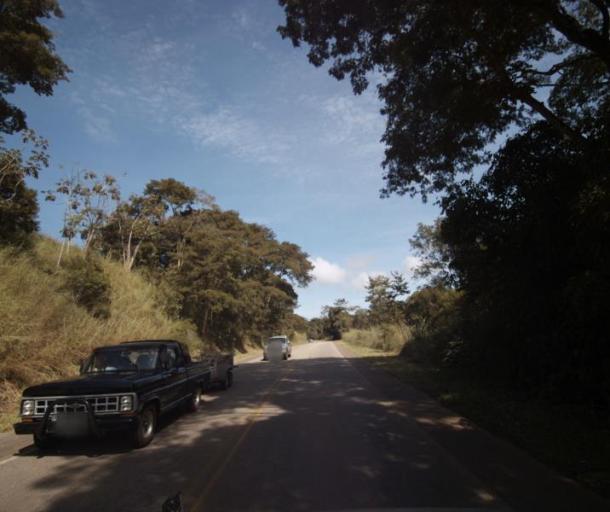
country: BR
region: Goias
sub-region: Abadiania
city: Abadiania
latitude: -16.1105
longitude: -48.8802
